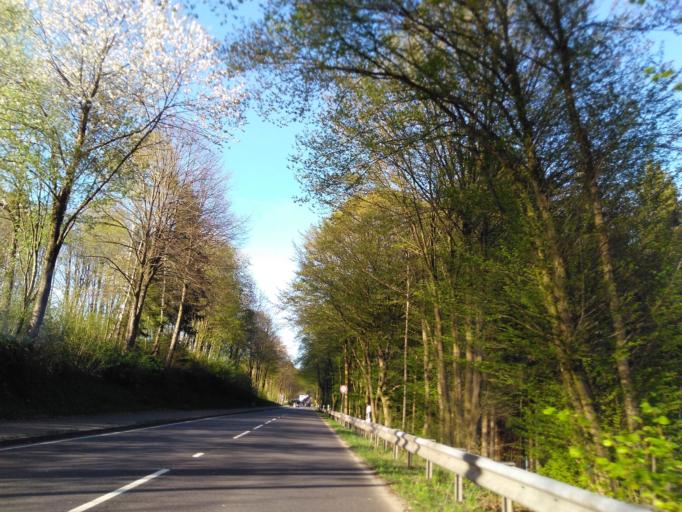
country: DE
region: North Rhine-Westphalia
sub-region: Regierungsbezirk Koln
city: Much
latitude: 50.9243
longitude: 7.4375
